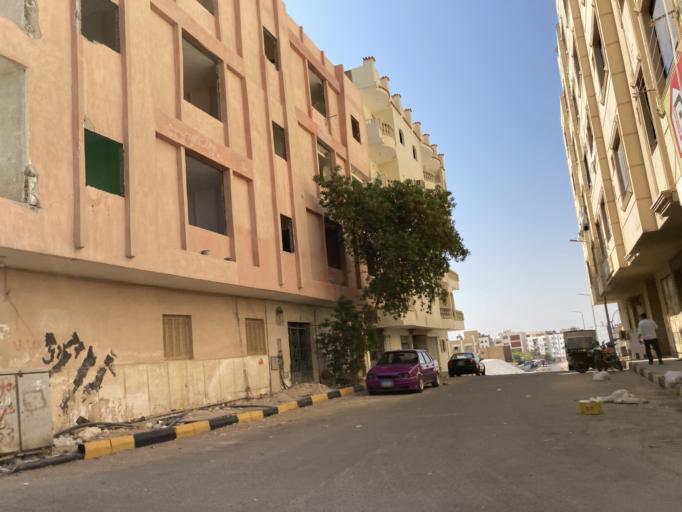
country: EG
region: Red Sea
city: Hurghada
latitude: 27.2501
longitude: 33.8324
